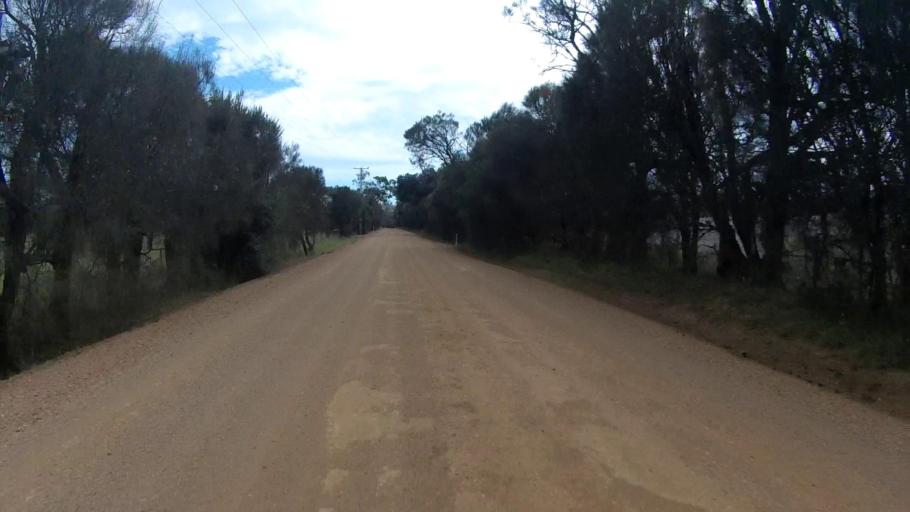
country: AU
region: Tasmania
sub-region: Clarence
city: Cambridge
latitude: -42.7039
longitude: 147.4574
